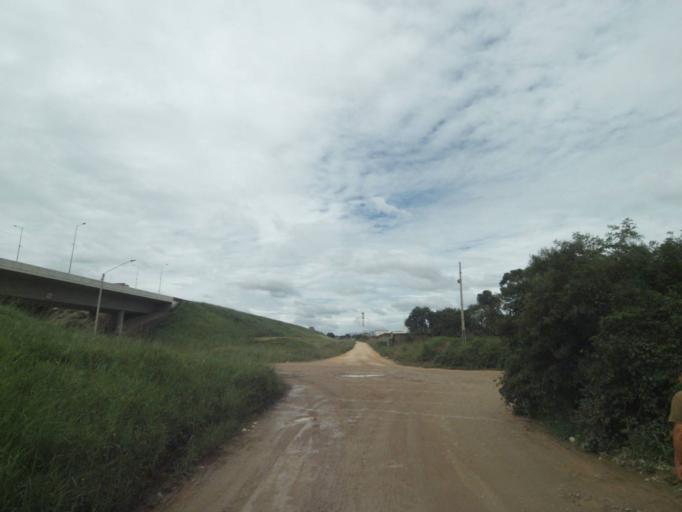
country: BR
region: Parana
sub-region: Sao Jose Dos Pinhais
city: Sao Jose dos Pinhais
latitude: -25.5338
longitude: -49.1471
